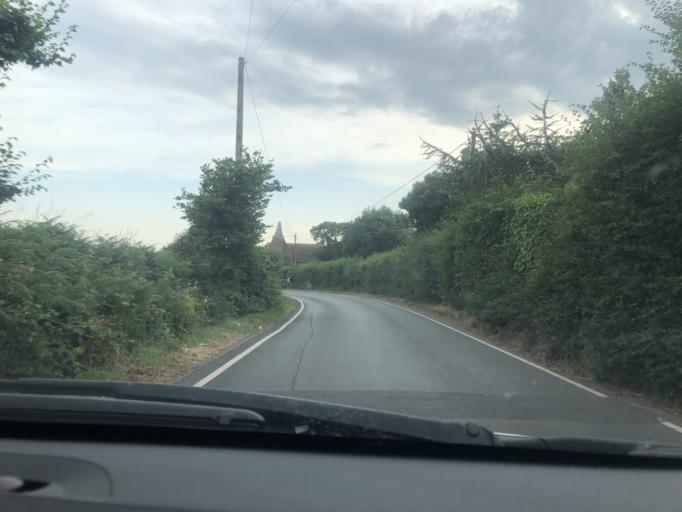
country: GB
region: England
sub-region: Kent
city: Sturry
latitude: 51.3252
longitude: 1.1444
